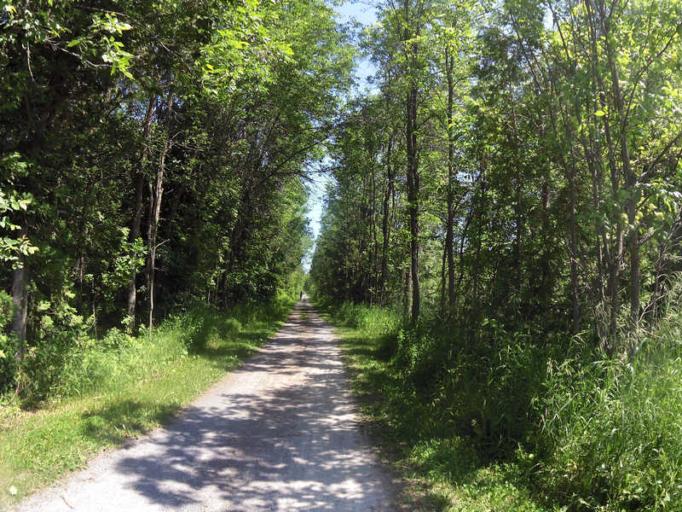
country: CA
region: Ontario
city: Peterborough
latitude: 44.3872
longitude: -78.2682
